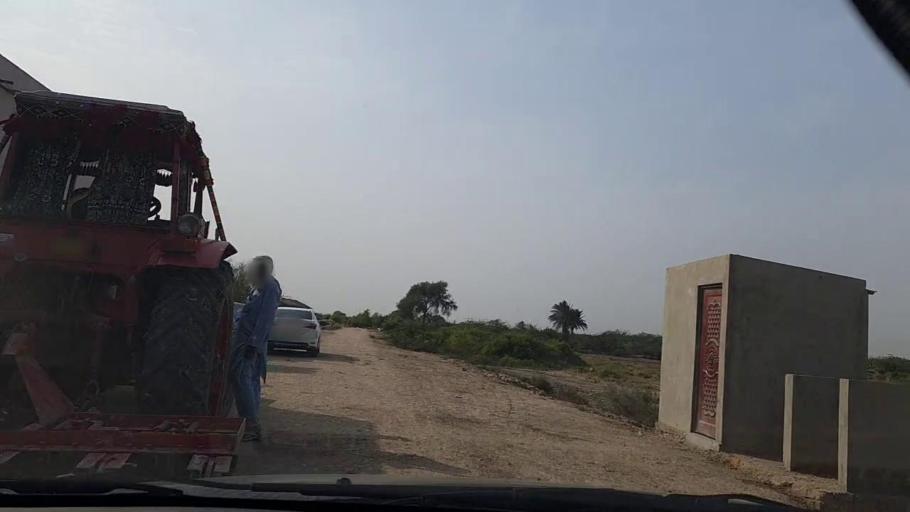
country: PK
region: Sindh
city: Thatta
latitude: 24.6101
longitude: 67.9517
